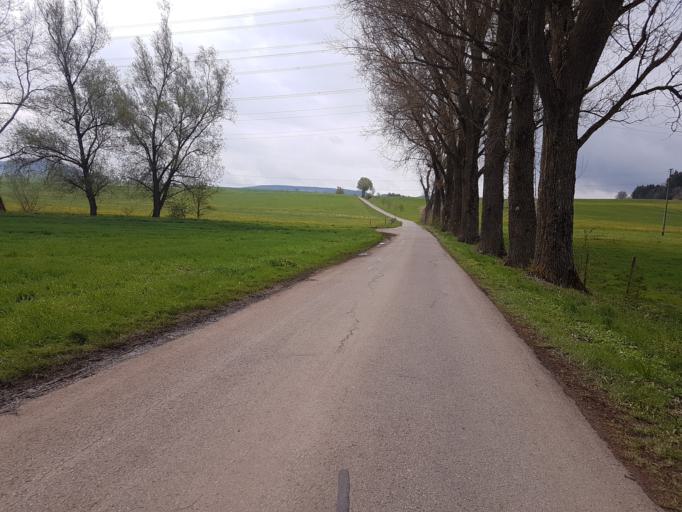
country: DE
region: Baden-Wuerttemberg
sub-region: Freiburg Region
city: Hufingen
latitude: 47.9141
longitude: 8.5177
